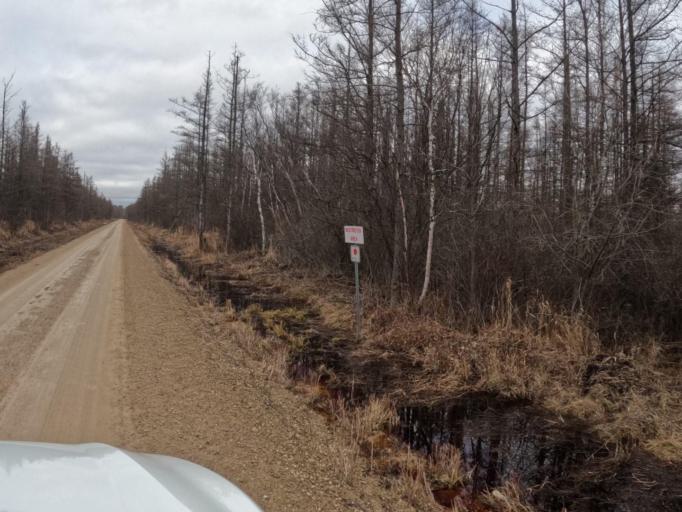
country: CA
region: Ontario
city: Shelburne
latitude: 43.8995
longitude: -80.4085
